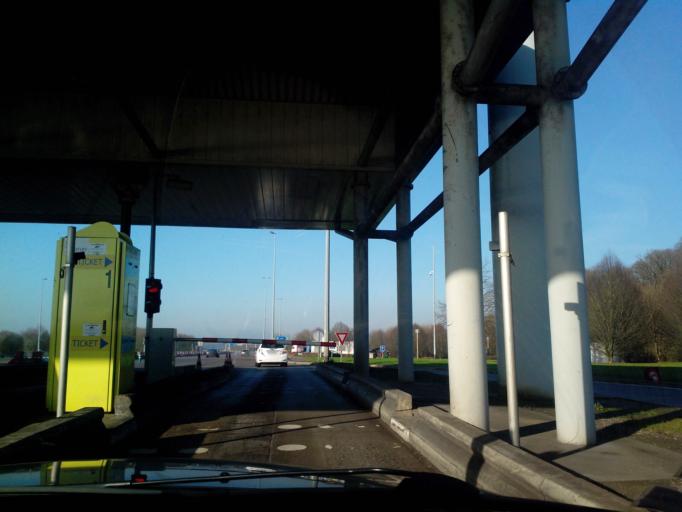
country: FR
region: Picardie
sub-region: Departement de l'Oise
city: Esches
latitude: 49.2054
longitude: 2.1693
